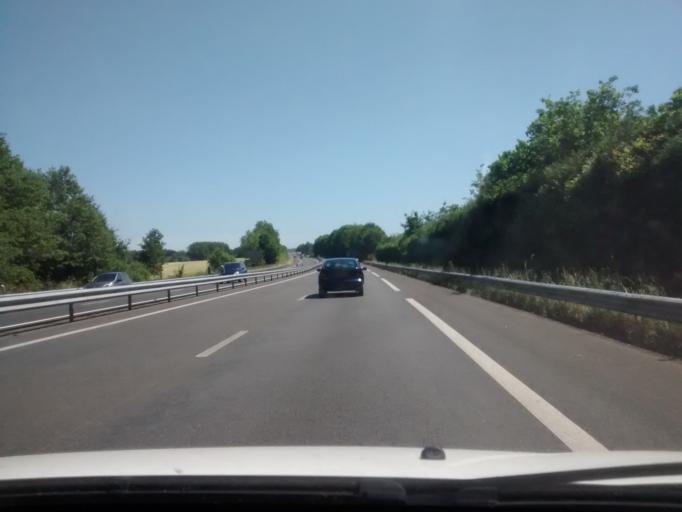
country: FR
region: Brittany
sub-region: Departement d'Ille-et-Vilaine
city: Tinteniac
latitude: 48.3328
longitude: -1.8585
